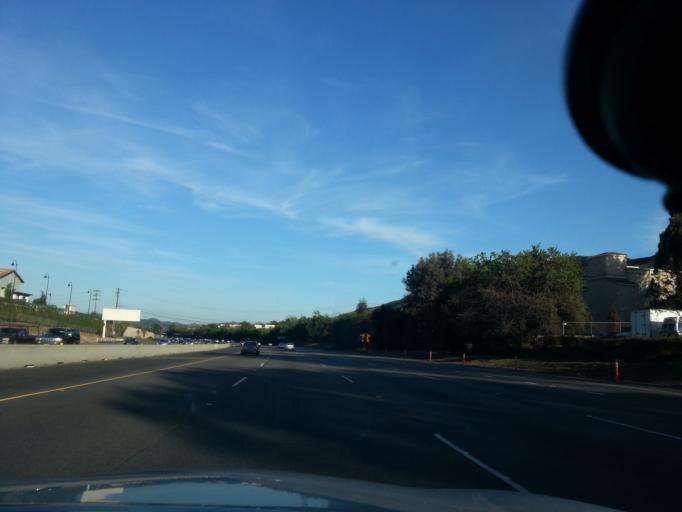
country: US
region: California
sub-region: Los Angeles County
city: Westlake Village
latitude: 34.1464
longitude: -118.7954
